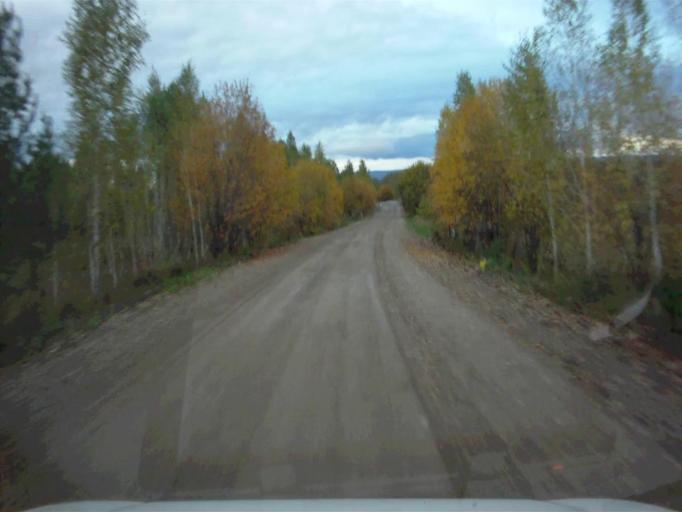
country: RU
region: Sverdlovsk
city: Mikhaylovsk
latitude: 56.2071
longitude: 59.2060
